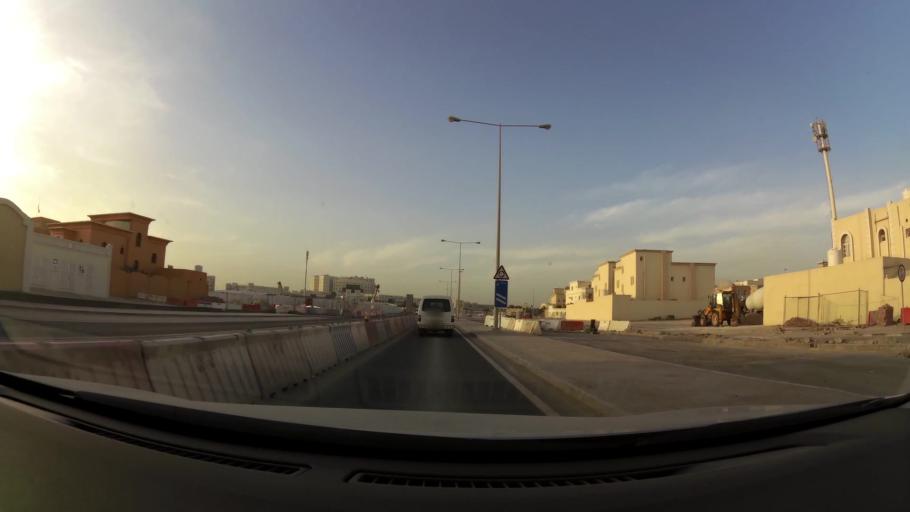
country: QA
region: Al Wakrah
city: Al Wakrah
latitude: 25.1623
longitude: 51.5904
